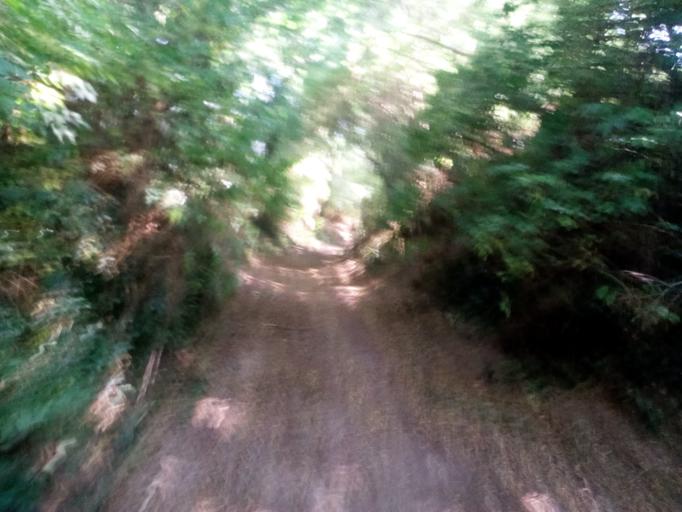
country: FR
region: Lower Normandy
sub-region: Departement du Calvados
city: Bernieres-sur-Mer
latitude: 49.3057
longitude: -0.4248
